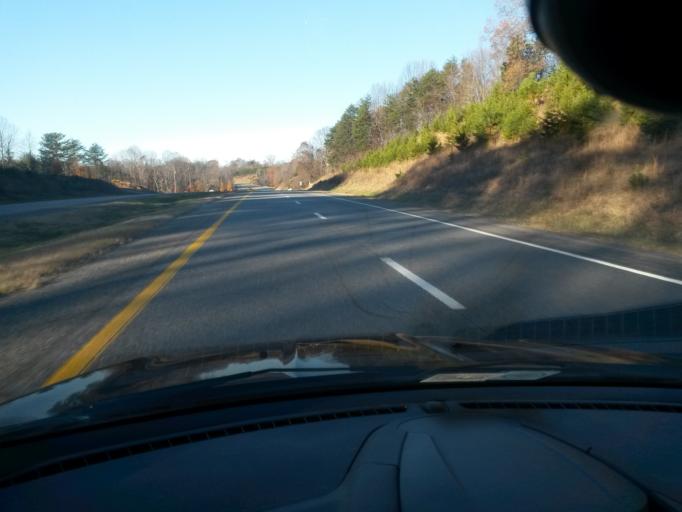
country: US
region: Virginia
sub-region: Henry County
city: Horse Pasture
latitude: 36.6035
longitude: -80.0656
